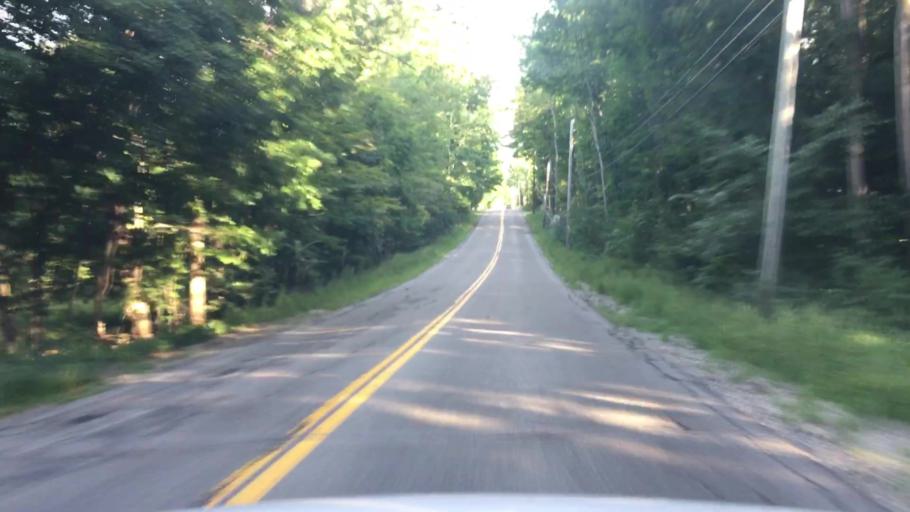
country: US
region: Maine
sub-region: Cumberland County
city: South Windham
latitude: 43.7152
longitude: -70.3912
